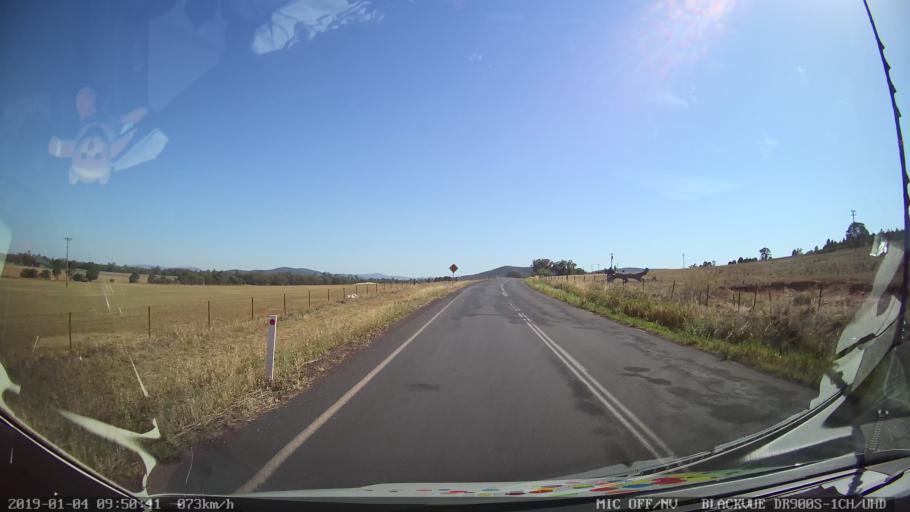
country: AU
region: New South Wales
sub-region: Cabonne
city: Canowindra
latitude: -33.5817
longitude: 148.4161
